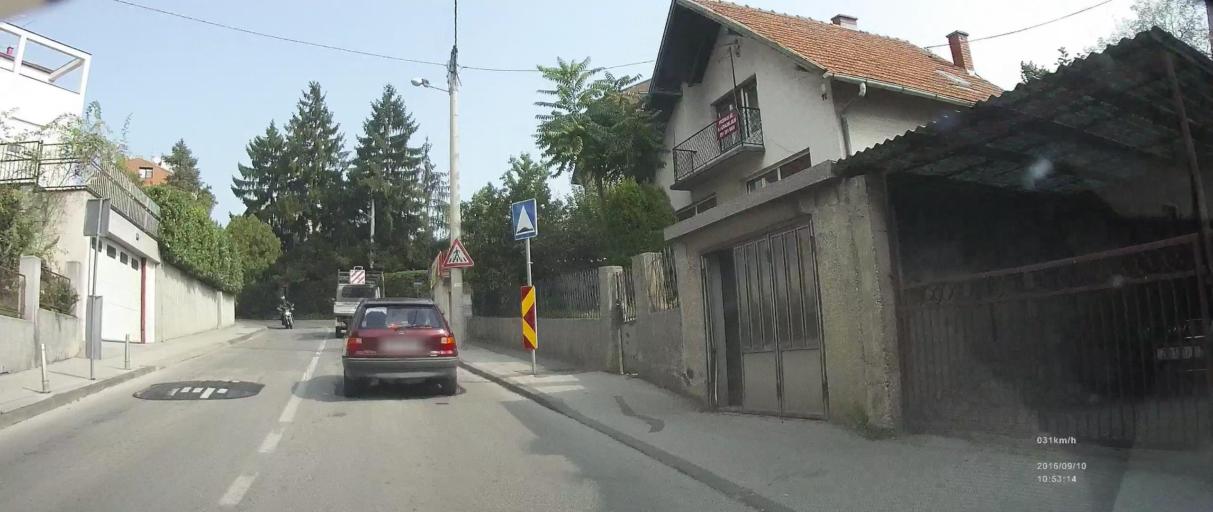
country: HR
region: Grad Zagreb
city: Zagreb - Centar
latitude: 45.8226
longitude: 15.9388
